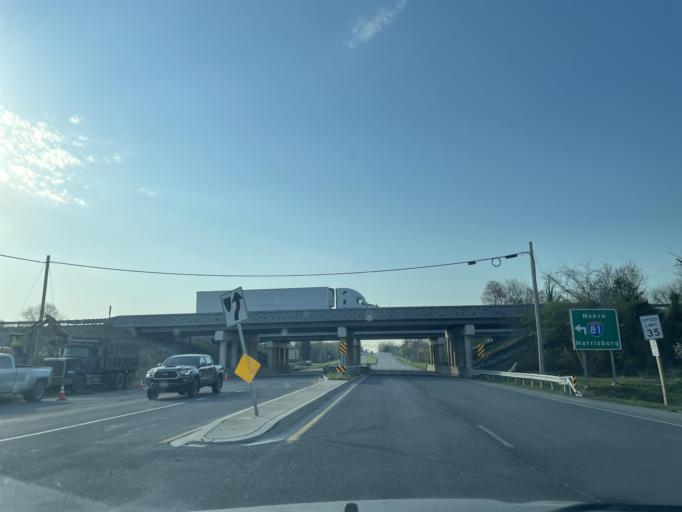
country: US
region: Maryland
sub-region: Washington County
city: Williamsport
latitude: 39.5882
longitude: -77.8167
